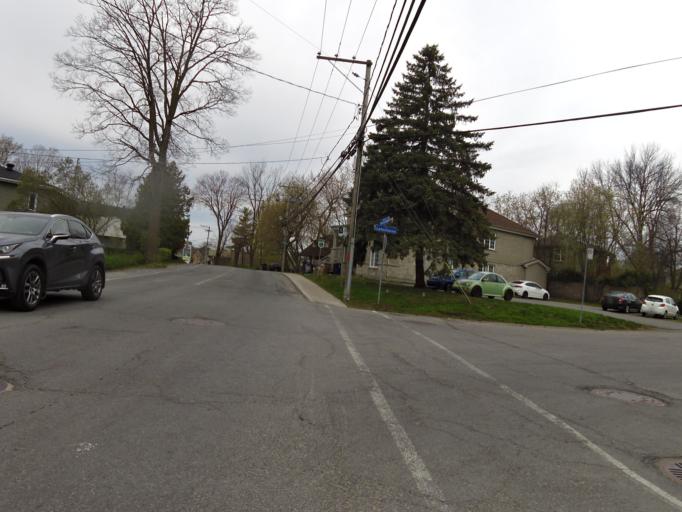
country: CA
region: Quebec
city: Dollard-Des Ormeaux
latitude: 45.5237
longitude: -73.8501
